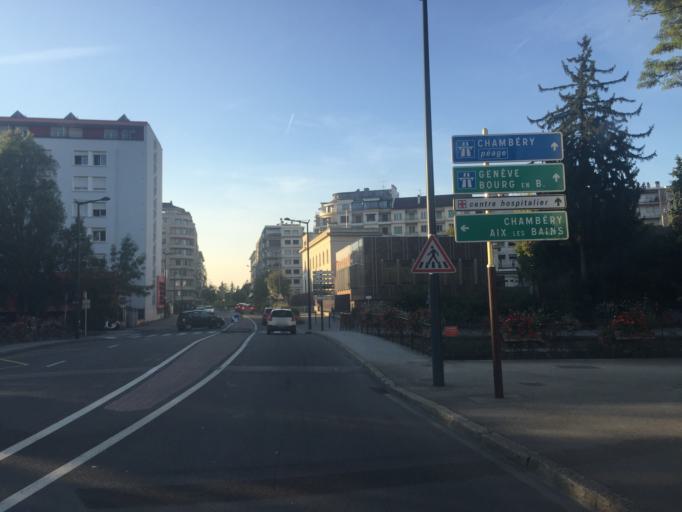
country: FR
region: Rhone-Alpes
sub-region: Departement de la Haute-Savoie
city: Annecy
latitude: 45.8979
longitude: 6.1196
